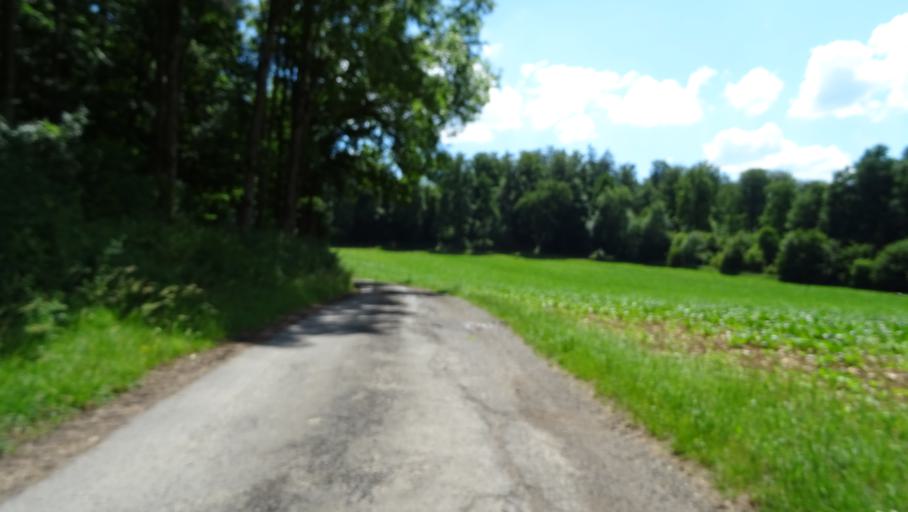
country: DE
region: Baden-Wuerttemberg
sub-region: Karlsruhe Region
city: Adelsheim
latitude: 49.4122
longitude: 9.3658
